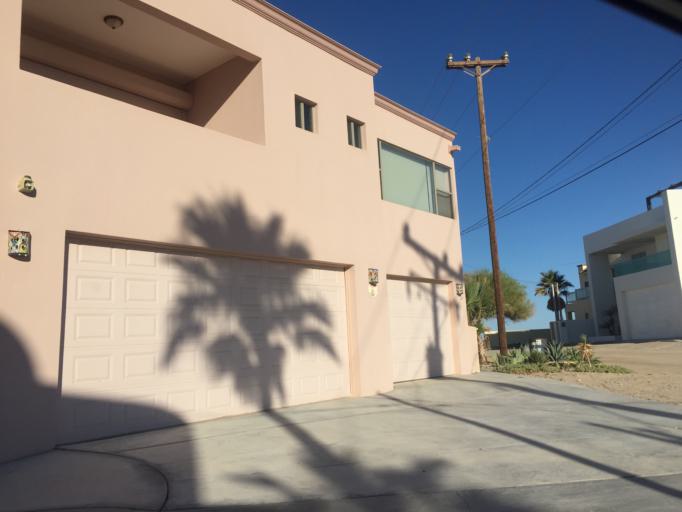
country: MX
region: Sonora
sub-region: Puerto Penasco
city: Puerto Penasco
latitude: 31.2923
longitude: -113.5050
